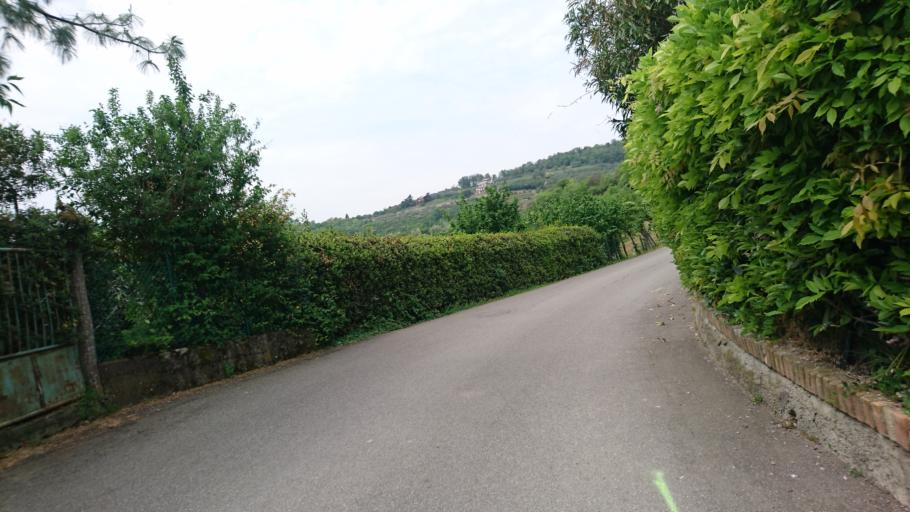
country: IT
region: Veneto
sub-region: Provincia di Padova
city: Arqua Petrarca
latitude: 45.2652
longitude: 11.7258
